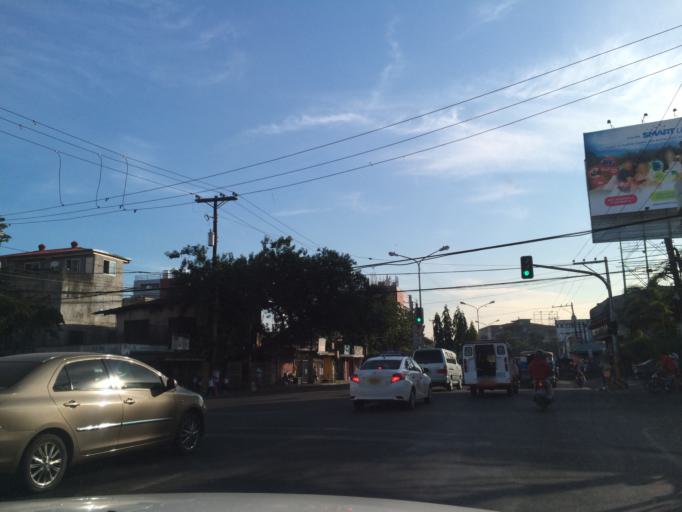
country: PH
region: Central Visayas
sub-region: Cebu City
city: Calero
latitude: 10.2969
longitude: 123.8860
